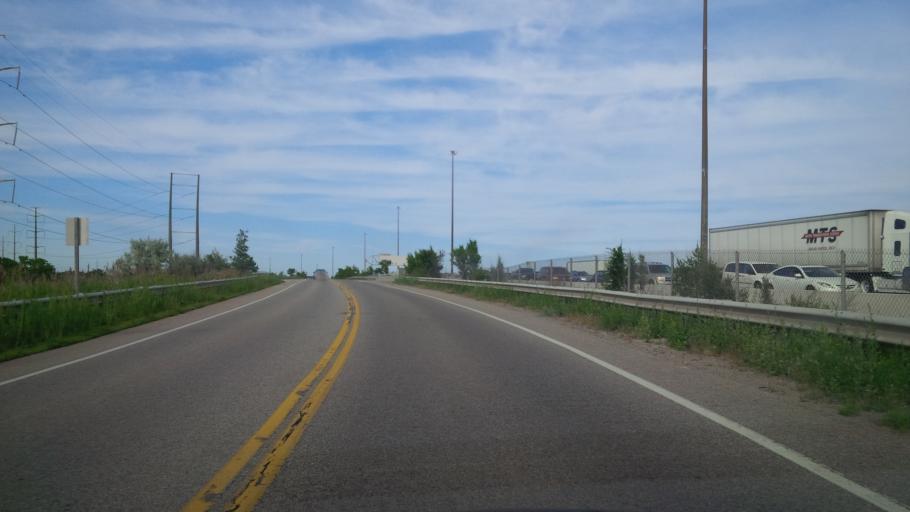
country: CA
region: Ontario
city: Burlington
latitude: 43.3454
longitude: -79.8151
